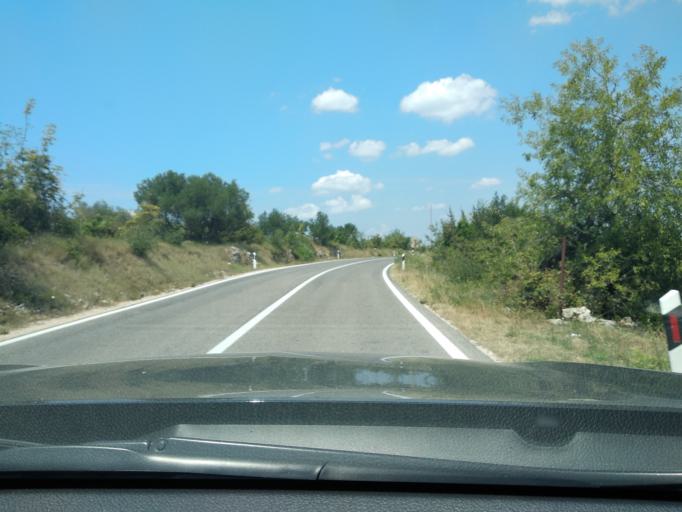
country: HR
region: Sibensko-Kniniska
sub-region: Grad Sibenik
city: Pirovac
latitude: 43.7995
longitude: 15.6754
